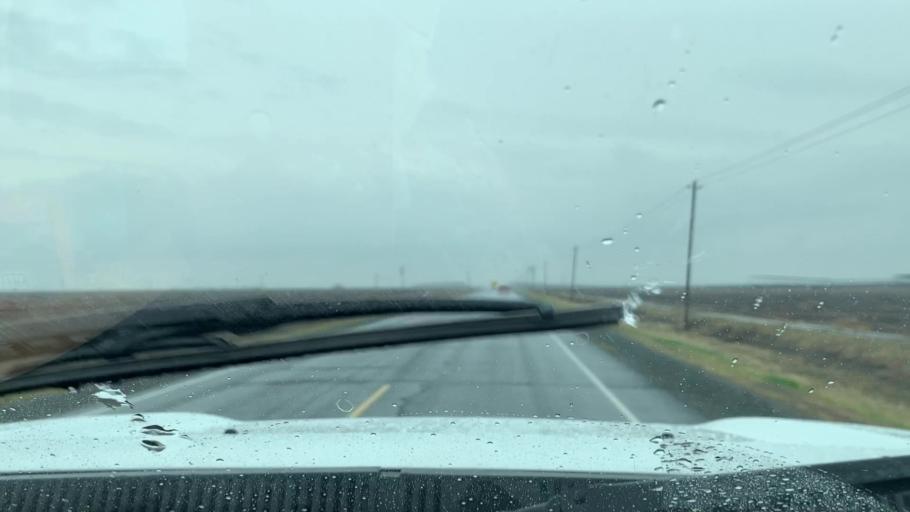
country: US
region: California
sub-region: Tulare County
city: Alpaugh
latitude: 35.9318
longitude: -119.4348
